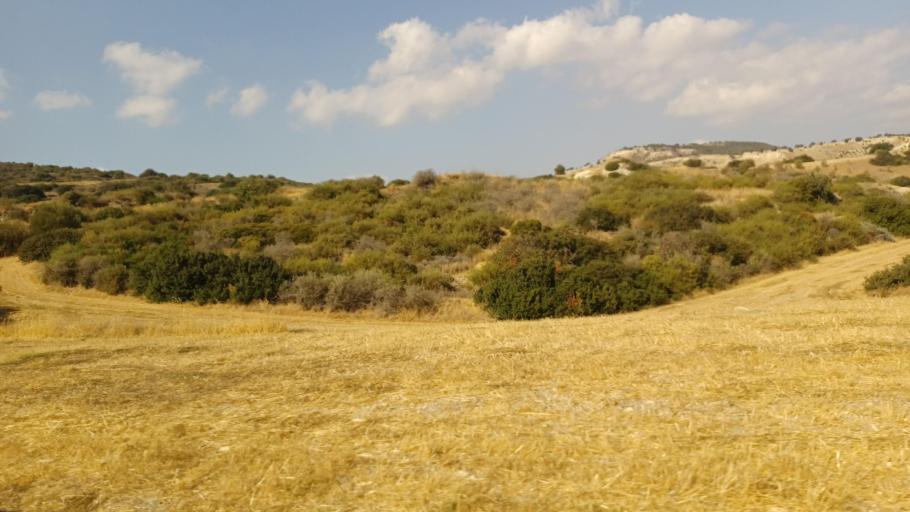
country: CY
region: Pafos
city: Polis
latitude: 34.9912
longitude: 32.4328
